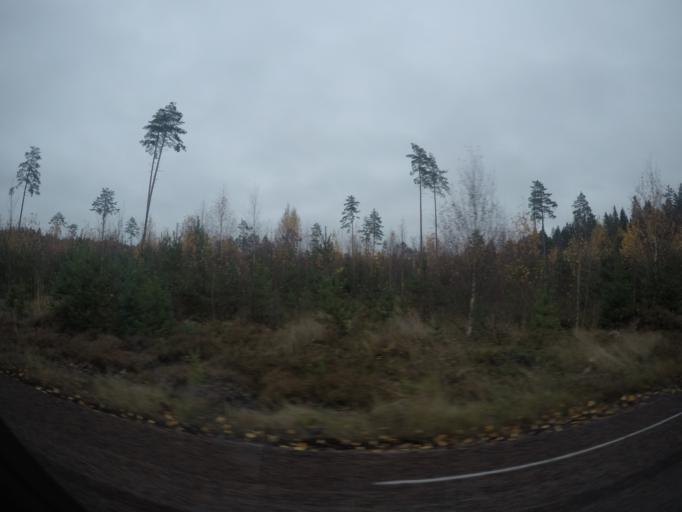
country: SE
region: Vaestmanland
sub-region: Surahammars Kommun
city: Surahammar
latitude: 59.6633
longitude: 16.0830
